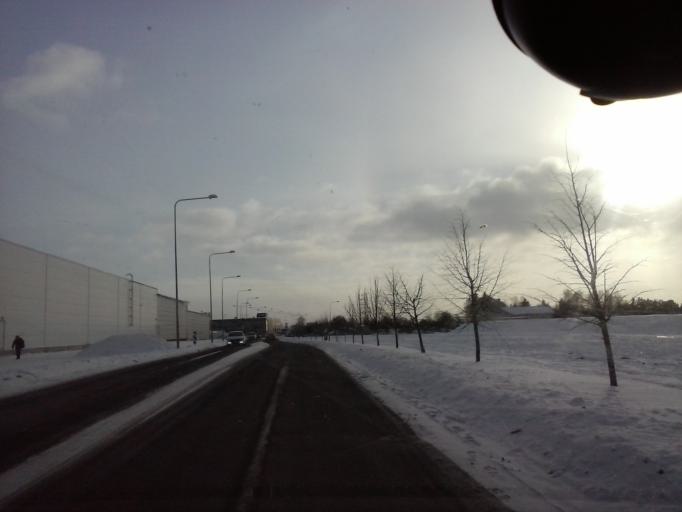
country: EE
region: Tartu
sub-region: Tartu linn
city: Tartu
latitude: 58.3618
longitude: 26.6745
